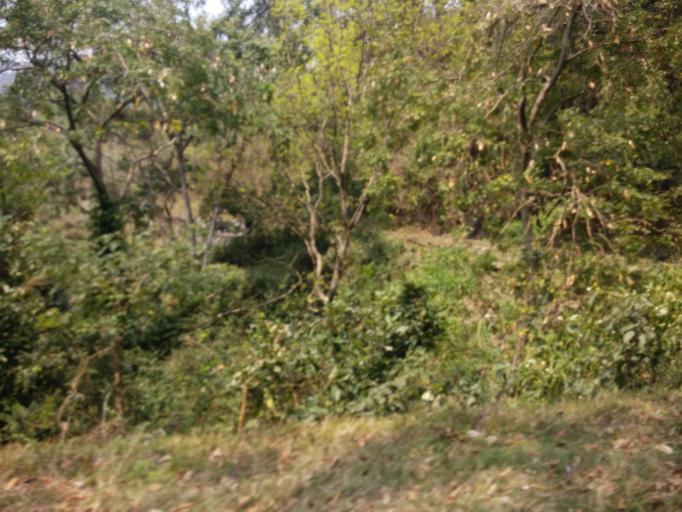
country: NP
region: Central Region
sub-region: Narayani Zone
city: Hitura
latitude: 27.5275
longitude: 85.0463
